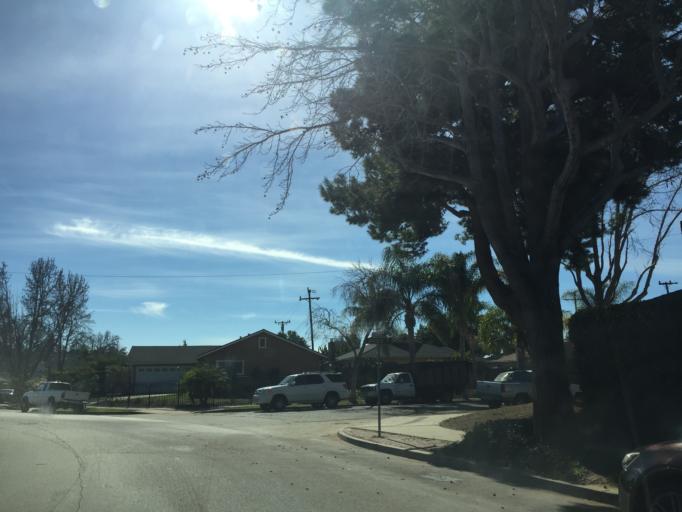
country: US
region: California
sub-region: Santa Barbara County
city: Goleta
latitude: 34.4409
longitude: -119.7848
